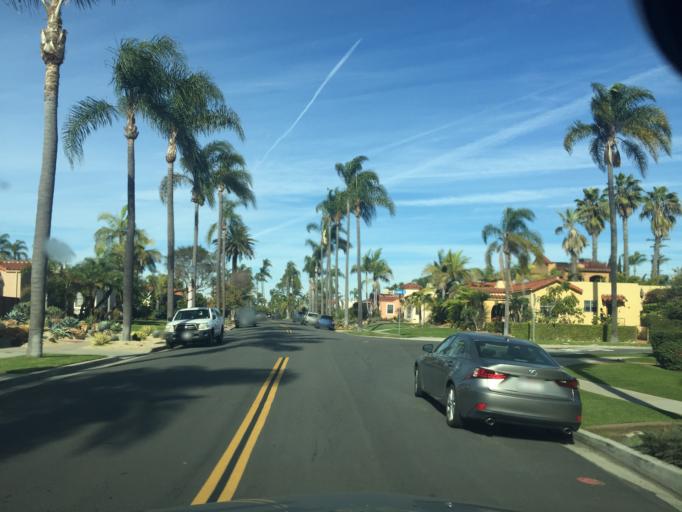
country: US
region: California
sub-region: San Diego County
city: San Diego
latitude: 32.7674
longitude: -117.1063
